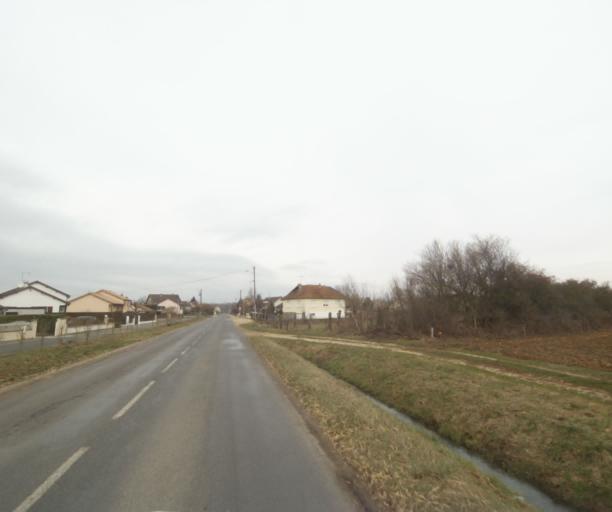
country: FR
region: Champagne-Ardenne
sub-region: Departement de la Haute-Marne
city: Villiers-en-Lieu
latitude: 48.6788
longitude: 4.8860
